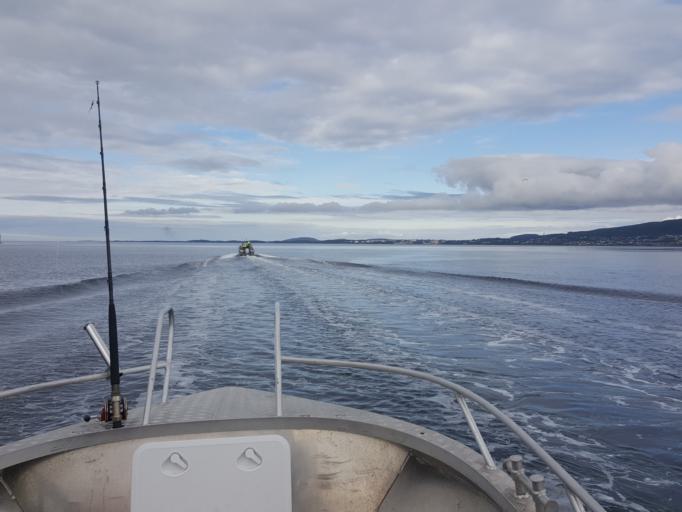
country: NO
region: Nordland
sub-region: Bodo
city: Lopsmarka
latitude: 67.2416
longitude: 14.5888
